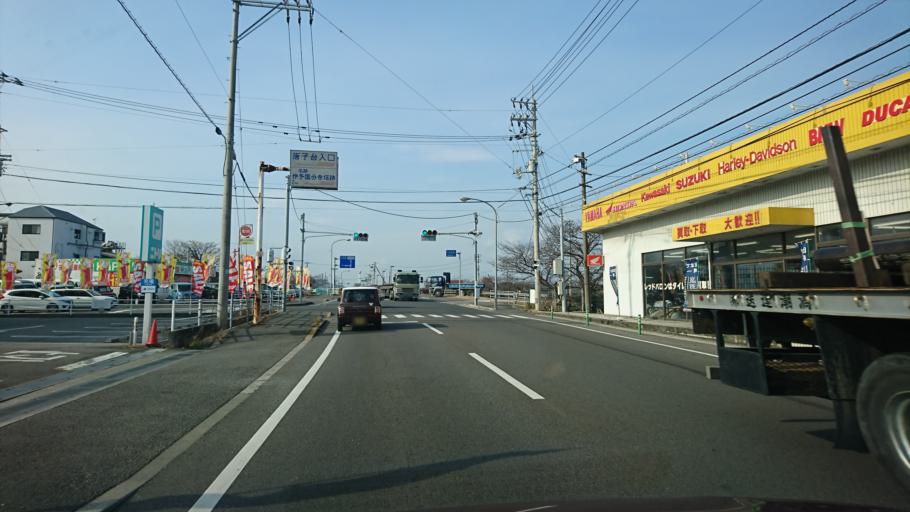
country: JP
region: Ehime
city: Saijo
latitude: 34.0369
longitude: 133.0327
